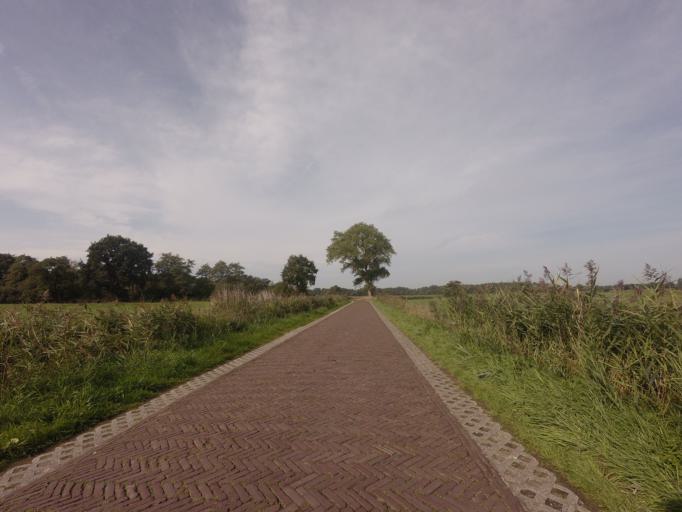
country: NL
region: Groningen
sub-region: Gemeente Leek
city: Leek
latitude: 53.1708
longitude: 6.4116
